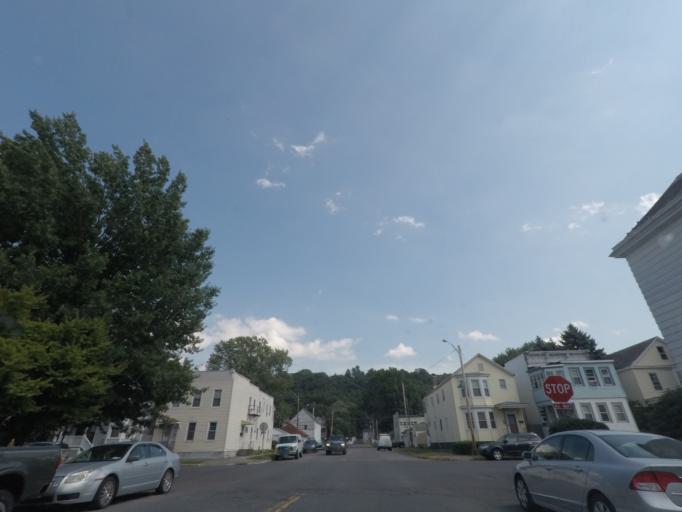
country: US
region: New York
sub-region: Saratoga County
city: Waterford
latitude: 42.7696
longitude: -73.6733
